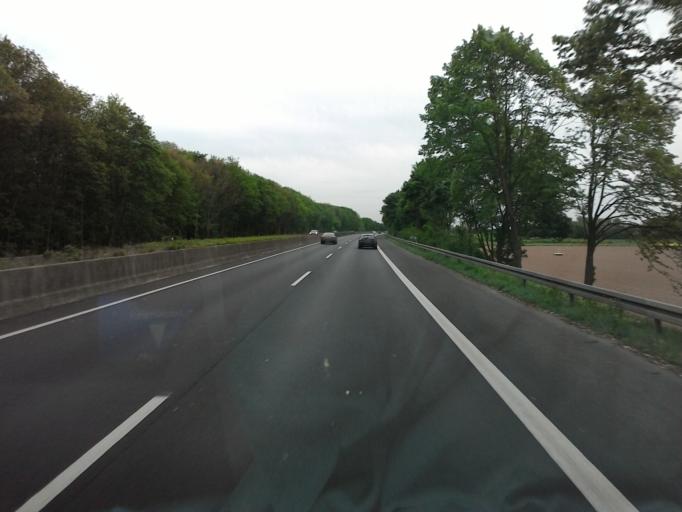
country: DE
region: North Rhine-Westphalia
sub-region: Regierungsbezirk Dusseldorf
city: Dormagen
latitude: 51.0646
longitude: 6.8318
